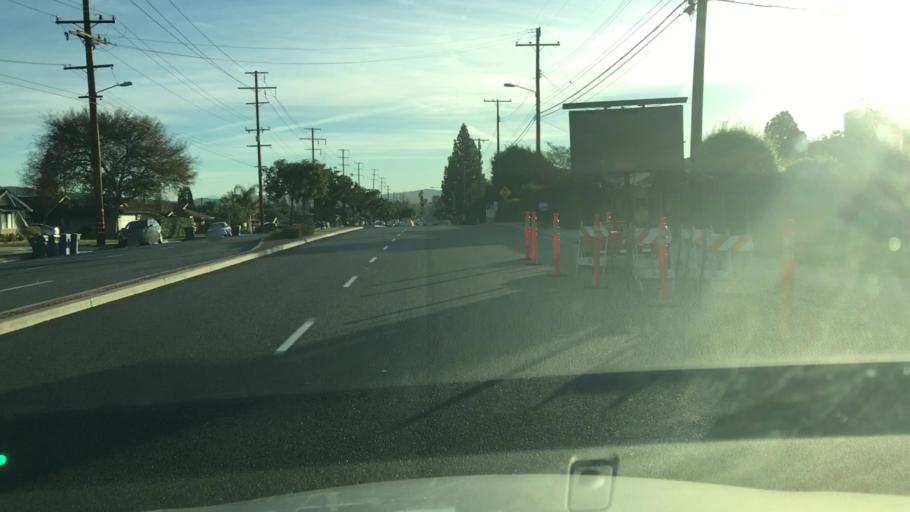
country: US
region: California
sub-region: Los Angeles County
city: East La Mirada
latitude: 33.9246
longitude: -117.9746
